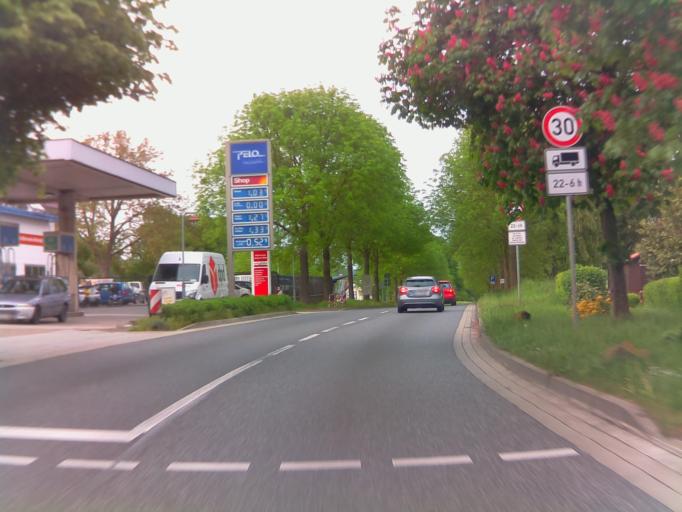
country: DE
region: Hesse
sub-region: Regierungsbezirk Kassel
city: Jesberg
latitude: 50.9964
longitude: 9.1457
